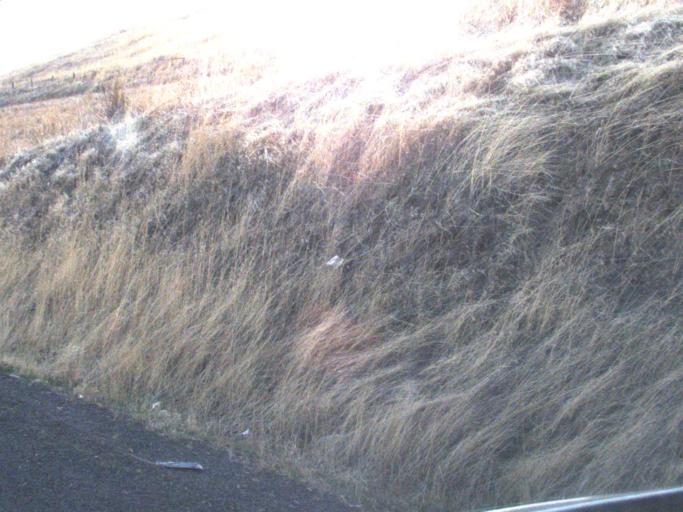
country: US
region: Washington
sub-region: Columbia County
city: Dayton
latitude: 46.4837
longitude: -117.9611
